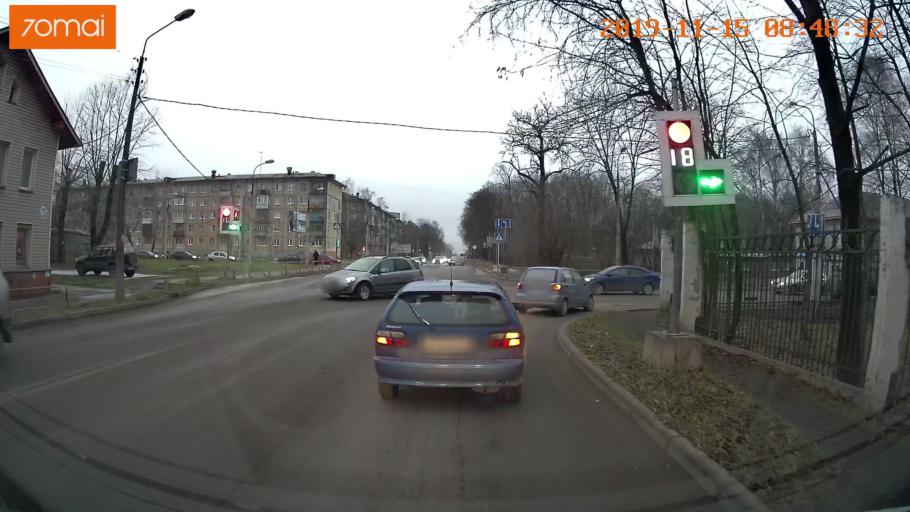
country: RU
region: Vologda
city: Cherepovets
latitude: 59.1222
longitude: 37.9185
